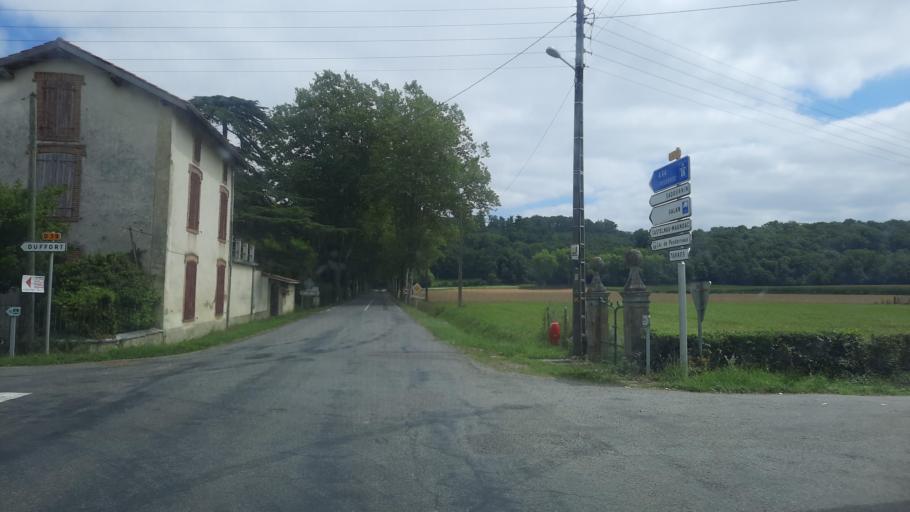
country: FR
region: Midi-Pyrenees
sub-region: Departement des Hautes-Pyrenees
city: Trie-sur-Baise
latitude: 43.3212
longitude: 0.3762
